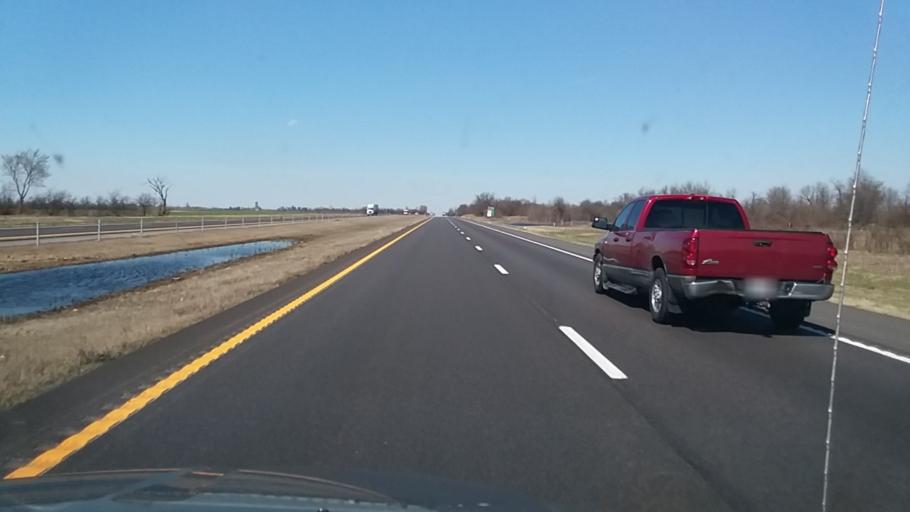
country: US
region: Missouri
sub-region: Scott County
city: Sikeston
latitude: 36.7981
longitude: -89.5319
